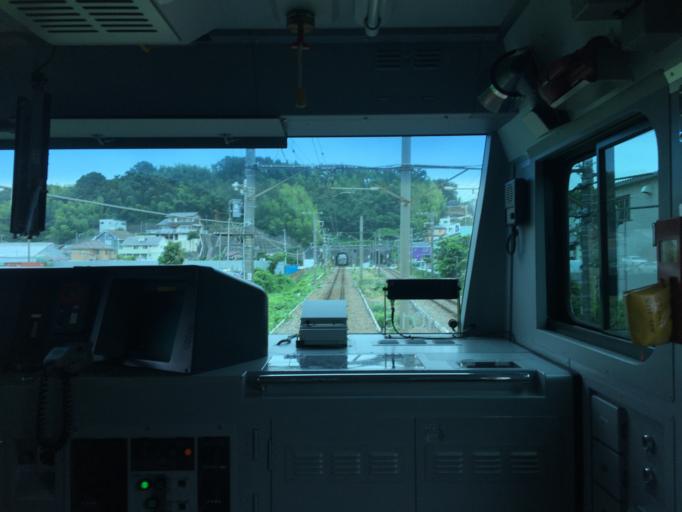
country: JP
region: Kanagawa
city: Yokohama
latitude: 35.5115
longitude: 139.5892
